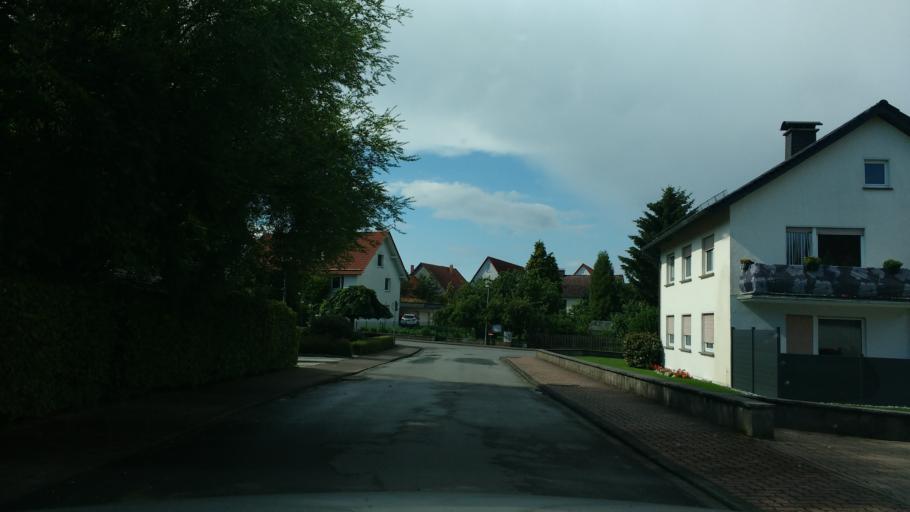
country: DE
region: North Rhine-Westphalia
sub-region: Regierungsbezirk Detmold
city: Barntrup
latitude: 52.0303
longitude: 9.1234
